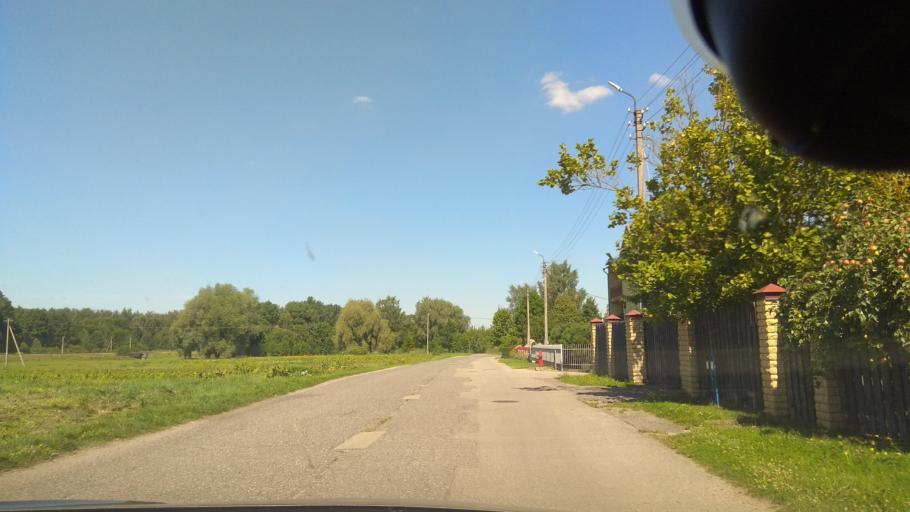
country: LT
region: Siauliu apskritis
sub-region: Joniskis
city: Joniskis
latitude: 56.2476
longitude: 23.6064
